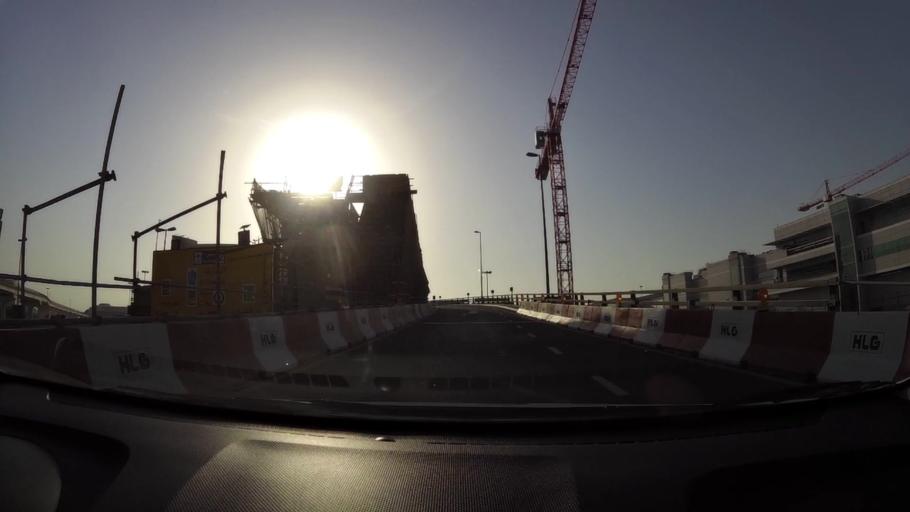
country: AE
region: Ash Shariqah
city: Sharjah
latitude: 25.2510
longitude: 55.3469
